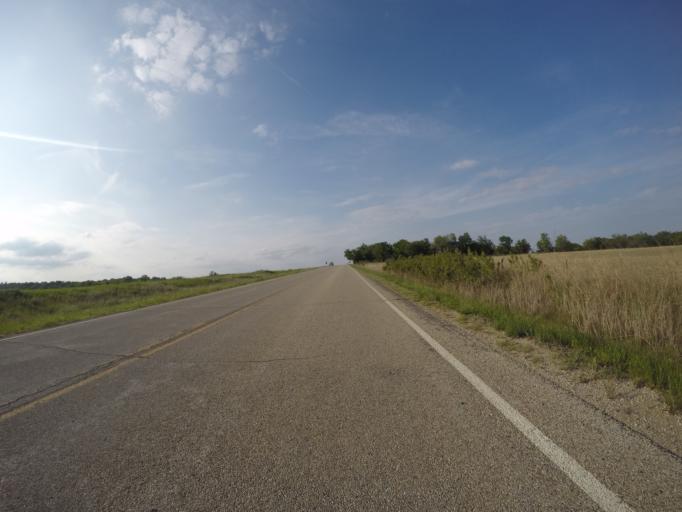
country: US
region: Kansas
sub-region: Pottawatomie County
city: Westmoreland
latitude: 39.4251
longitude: -96.6069
